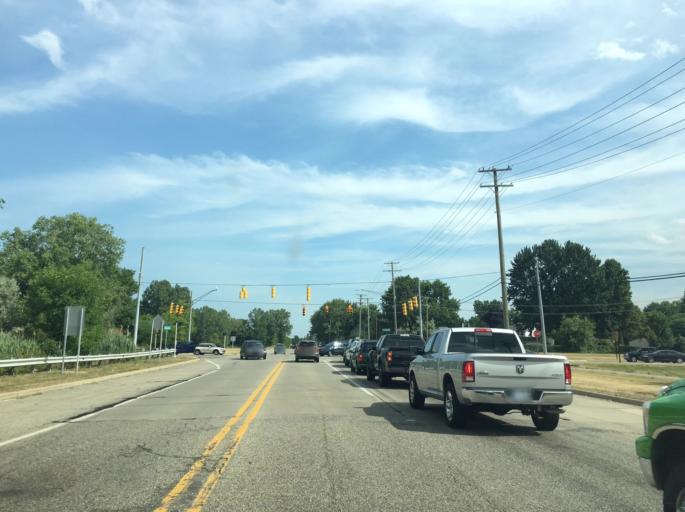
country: US
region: Michigan
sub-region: Macomb County
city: Sterling Heights
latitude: 42.5823
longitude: -82.9961
